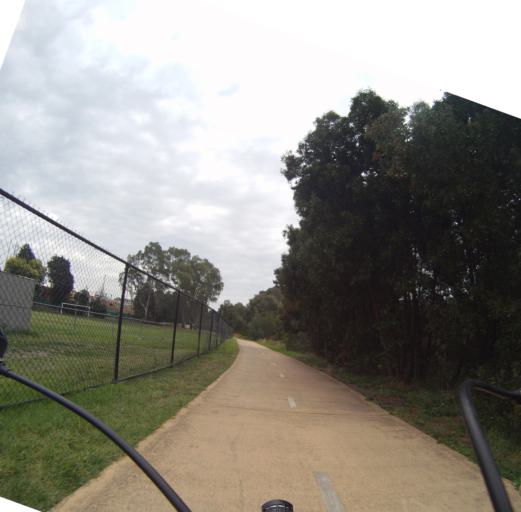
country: AU
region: Victoria
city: Brunswick East
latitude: -37.7736
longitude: 144.9863
